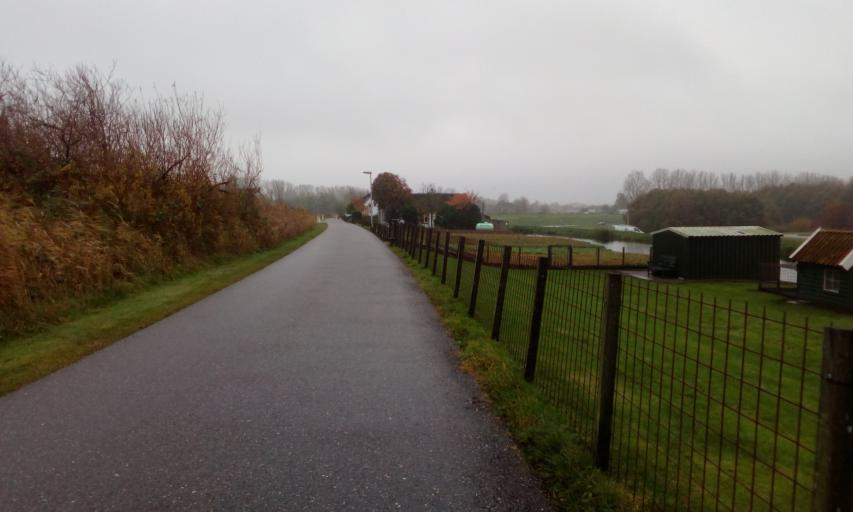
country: NL
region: South Holland
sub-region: Gemeente Lansingerland
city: Bleiswijk
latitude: 51.9822
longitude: 4.5487
